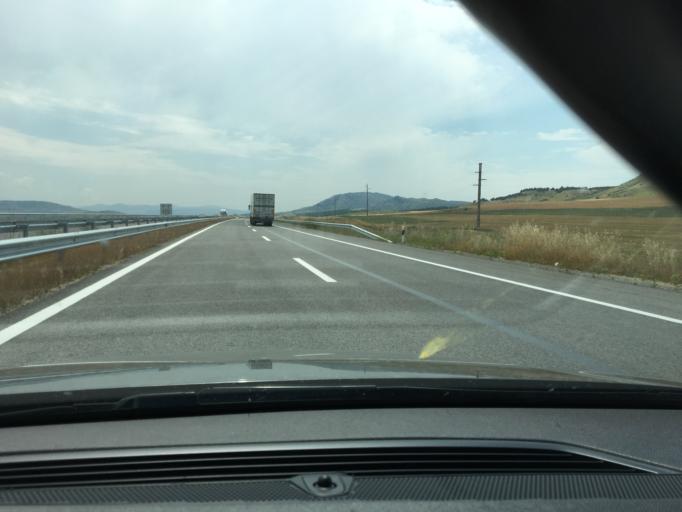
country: MK
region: Sveti Nikole
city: Sveti Nikole
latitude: 41.8062
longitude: 22.0661
